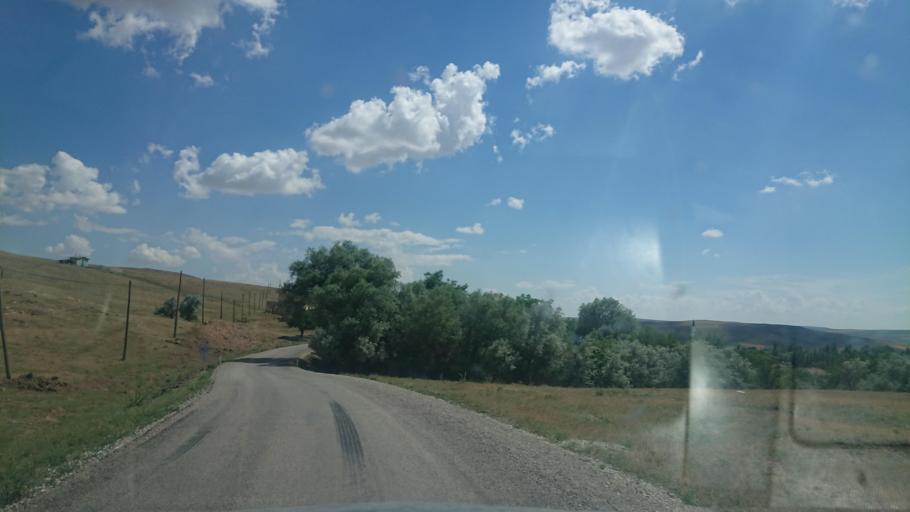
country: TR
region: Aksaray
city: Agacoren
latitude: 38.8329
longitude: 33.7988
